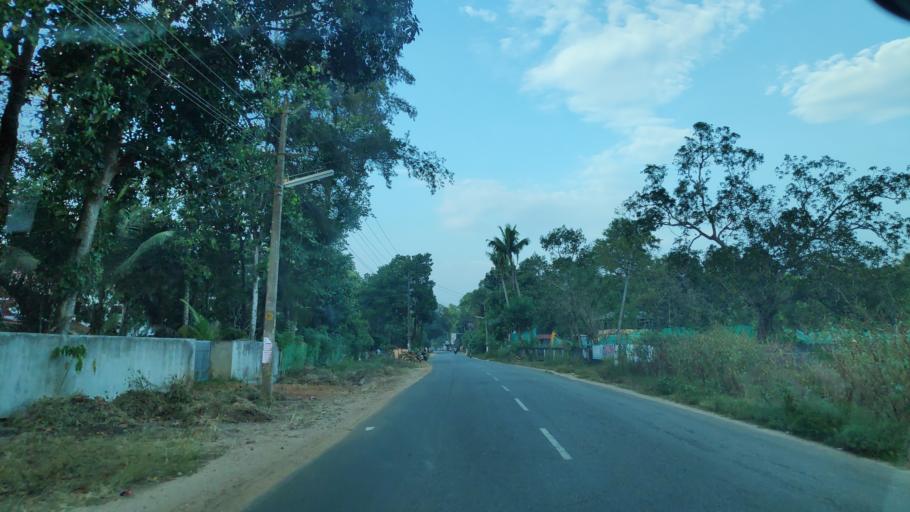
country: IN
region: Kerala
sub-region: Alappuzha
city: Shertallai
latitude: 9.6325
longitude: 76.3707
